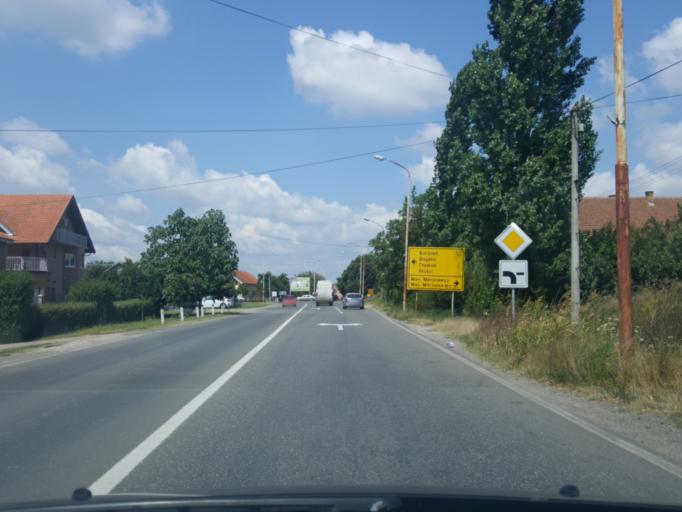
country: RS
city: Macvanska Mitrovica
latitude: 44.9555
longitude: 19.6014
